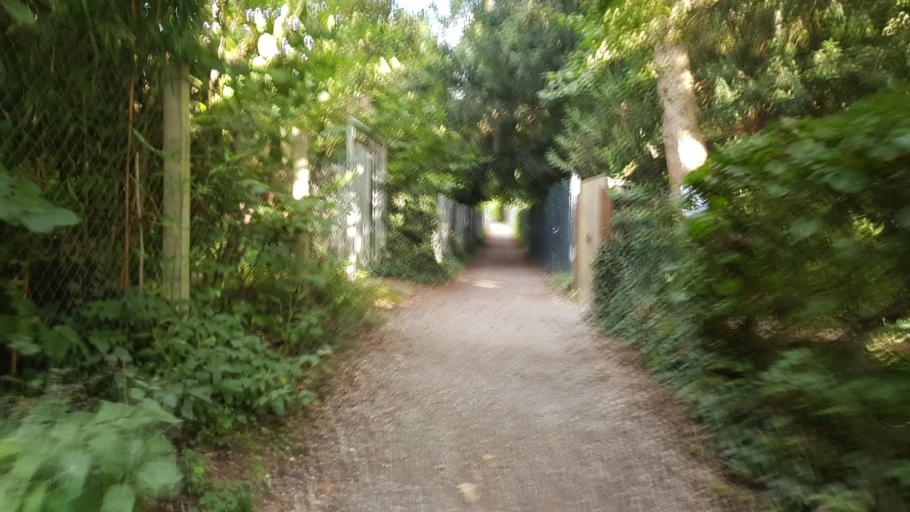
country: DE
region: Baden-Wuerttemberg
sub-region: Tuebingen Region
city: Friedrichshafen
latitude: 47.6550
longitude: 9.4532
